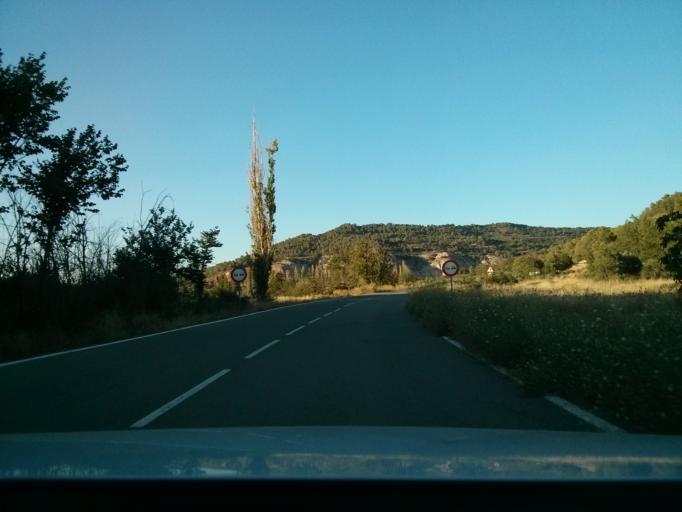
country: ES
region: Castille-La Mancha
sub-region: Provincia de Guadalajara
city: Chillaron del Rey
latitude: 40.5886
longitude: -2.7012
